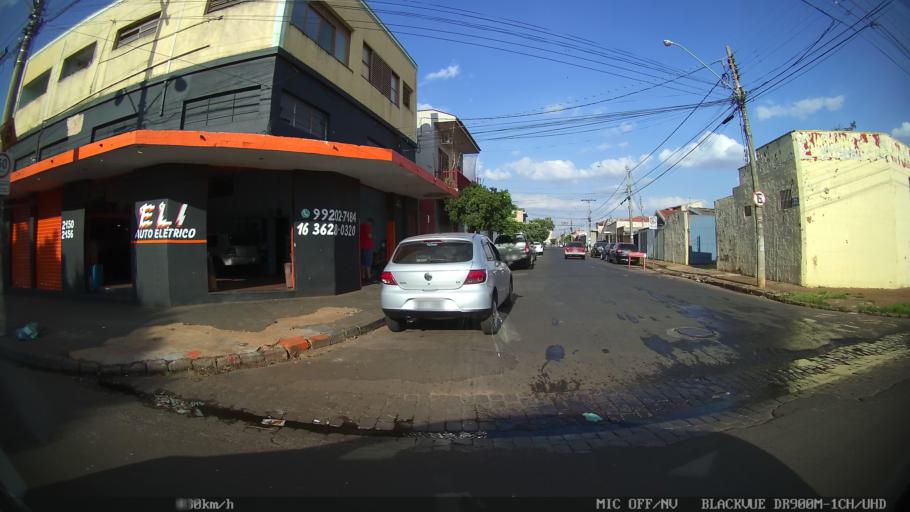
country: BR
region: Sao Paulo
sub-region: Ribeirao Preto
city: Ribeirao Preto
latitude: -21.1504
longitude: -47.8038
